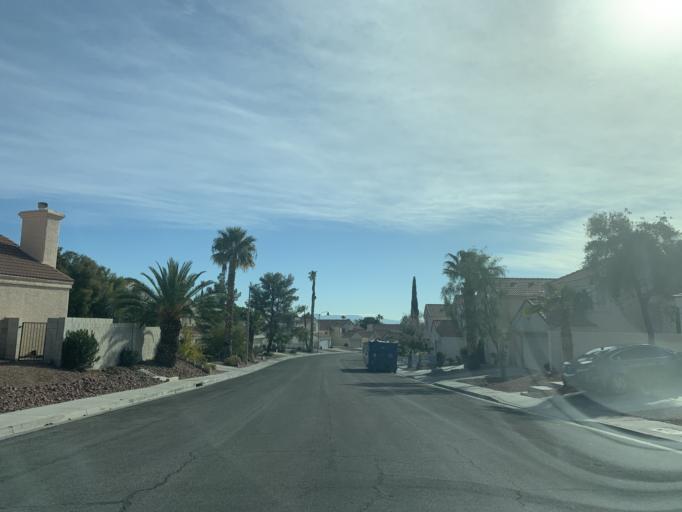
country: US
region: Nevada
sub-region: Clark County
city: Summerlin South
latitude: 36.1321
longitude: -115.2858
